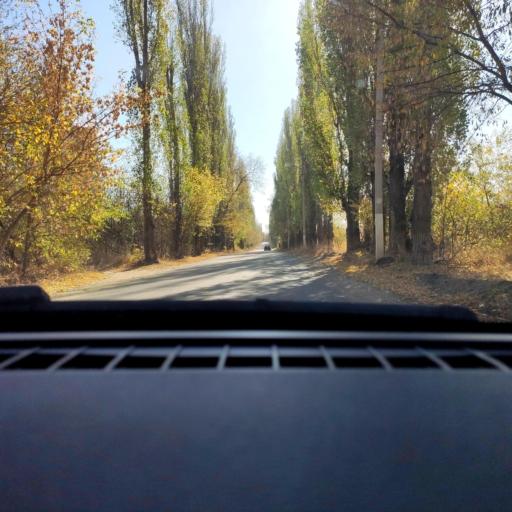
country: RU
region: Voronezj
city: Novaya Usman'
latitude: 51.6449
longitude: 39.3045
